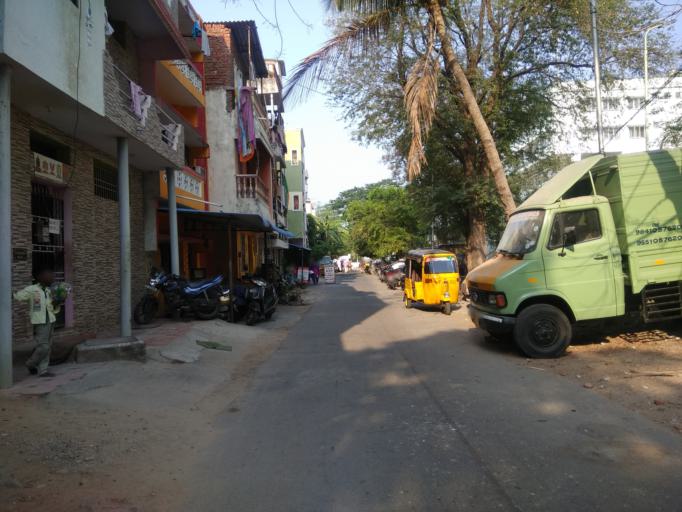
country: IN
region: Tamil Nadu
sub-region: Chennai
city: Gandhi Nagar
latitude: 13.0251
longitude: 80.2316
